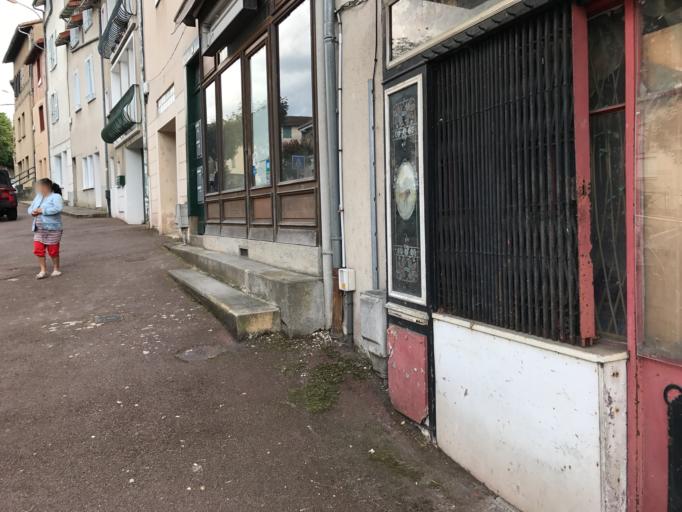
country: FR
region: Limousin
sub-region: Departement de la Haute-Vienne
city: Limoges
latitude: 45.8286
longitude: 1.2721
